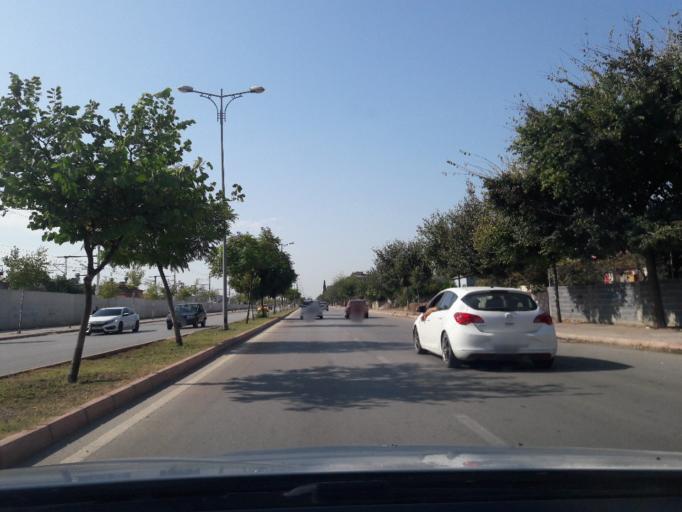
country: TR
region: Adana
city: Seyhan
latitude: 37.0019
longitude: 35.3091
